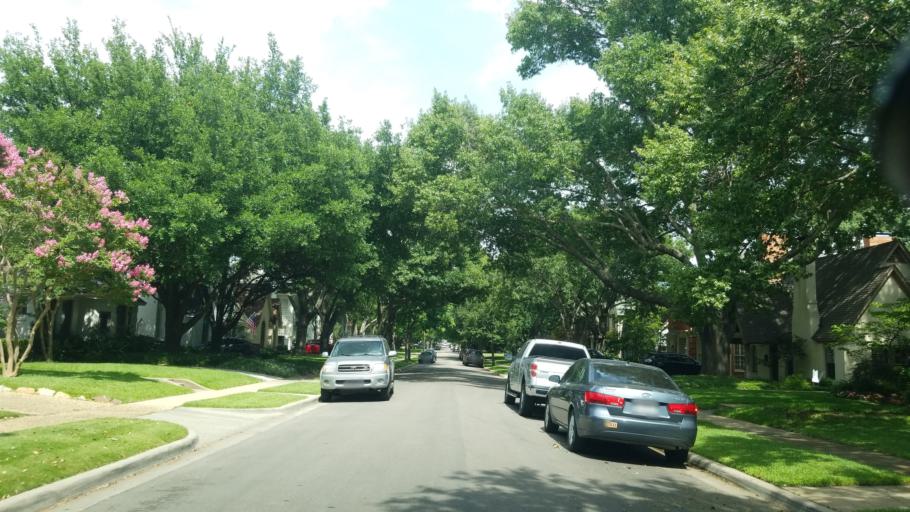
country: US
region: Texas
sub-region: Dallas County
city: University Park
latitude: 32.8521
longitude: -96.8022
